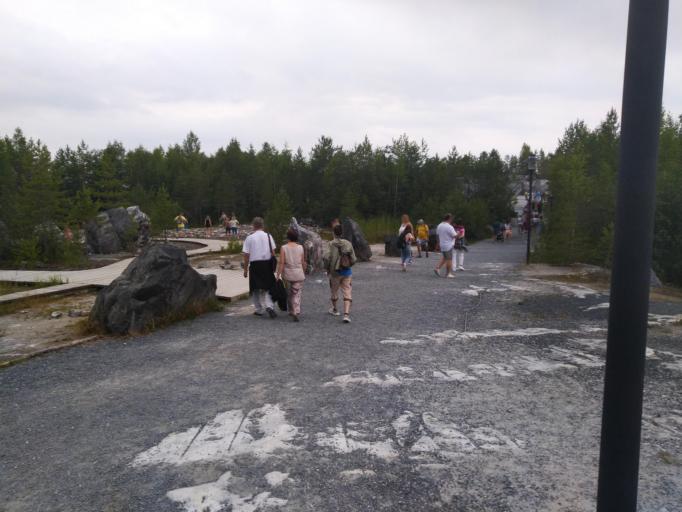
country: RU
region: Republic of Karelia
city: Ruskeala
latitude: 61.9488
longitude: 30.5745
